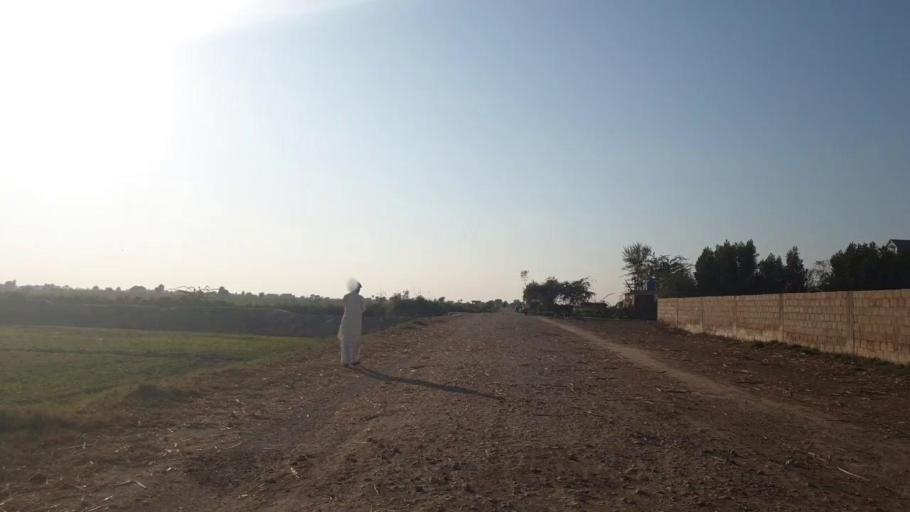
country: PK
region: Sindh
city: Shahpur Chakar
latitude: 26.0606
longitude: 68.6694
